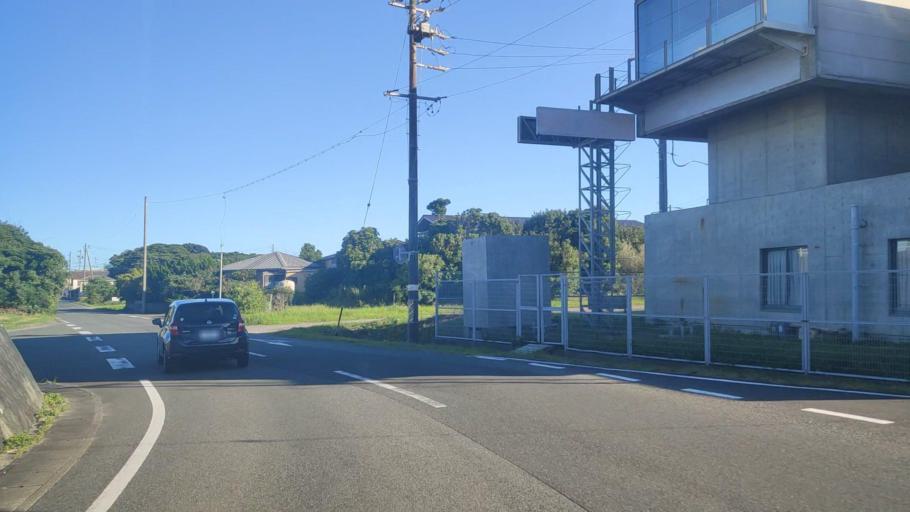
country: JP
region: Mie
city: Toba
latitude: 34.3201
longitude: 136.8826
